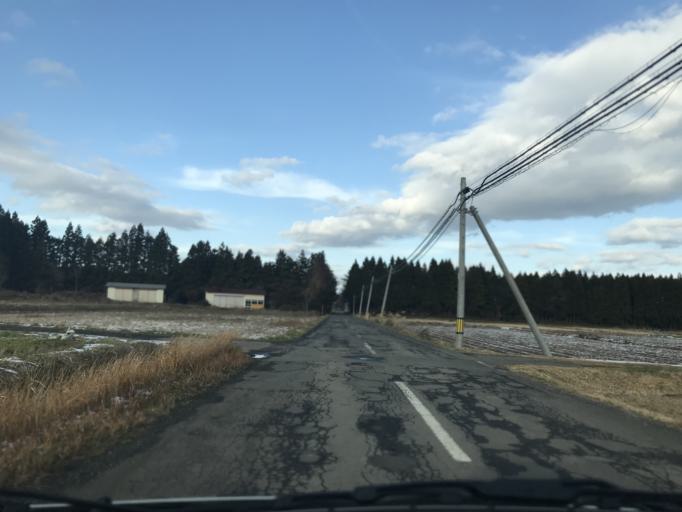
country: JP
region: Iwate
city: Kitakami
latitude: 39.2286
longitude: 141.0479
